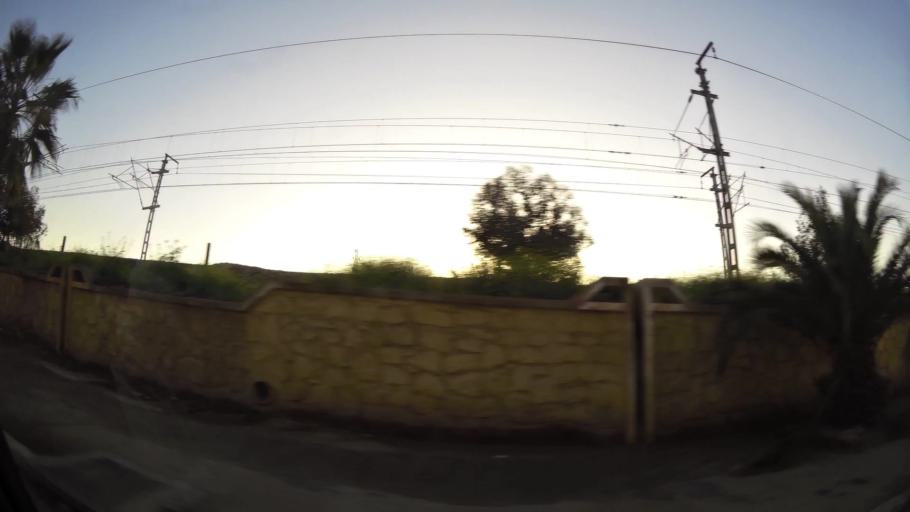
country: MA
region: Chaouia-Ouardigha
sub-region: Settat Province
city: Settat
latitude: 32.9847
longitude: -7.6214
